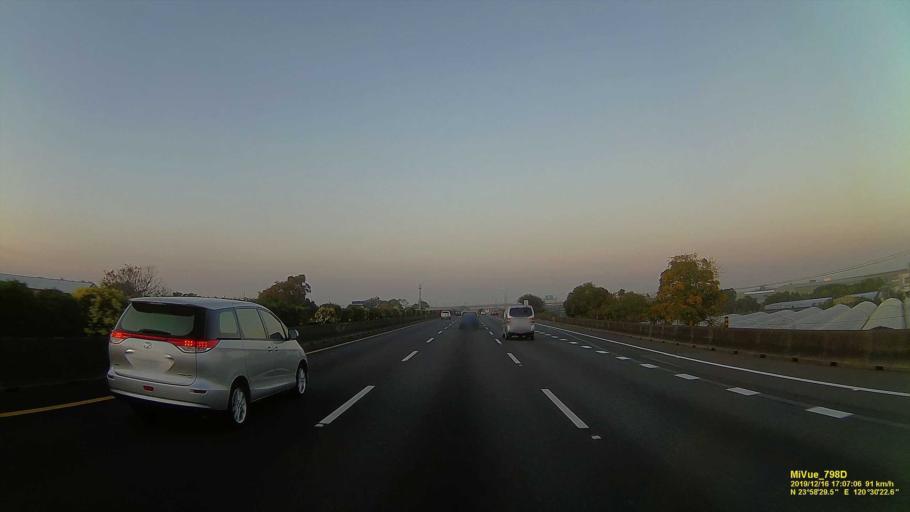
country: TW
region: Taiwan
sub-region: Changhua
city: Chang-hua
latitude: 23.9751
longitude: 120.5060
